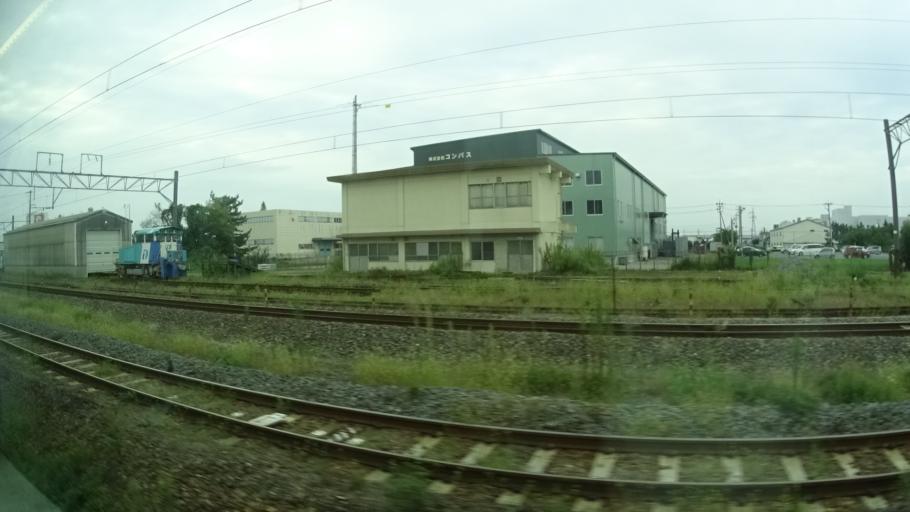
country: JP
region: Yamagata
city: Tsuruoka
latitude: 38.7399
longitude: 139.8380
